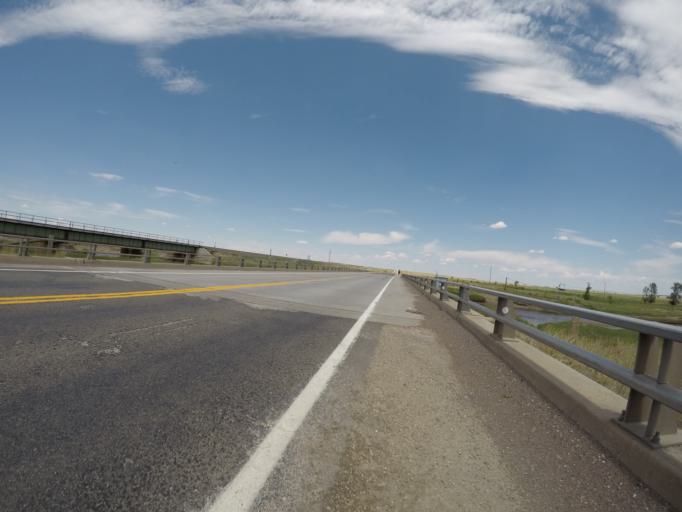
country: US
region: Wyoming
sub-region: Albany County
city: Laramie
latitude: 41.5543
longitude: -105.6829
